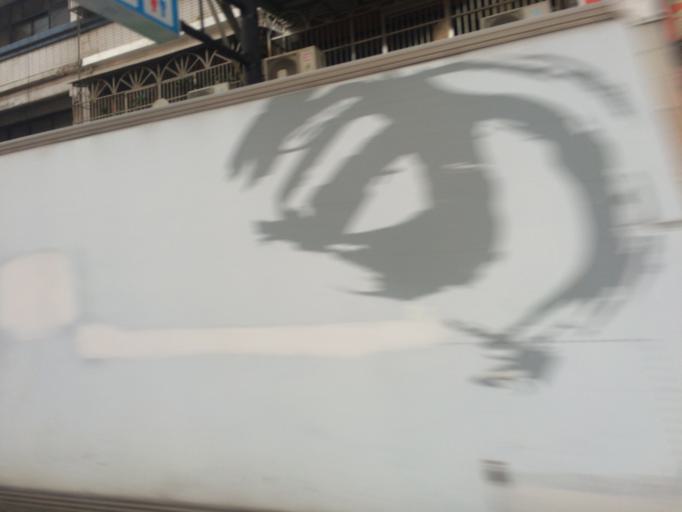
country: TW
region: Taiwan
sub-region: Hsinchu
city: Hsinchu
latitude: 24.7095
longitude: 120.9241
